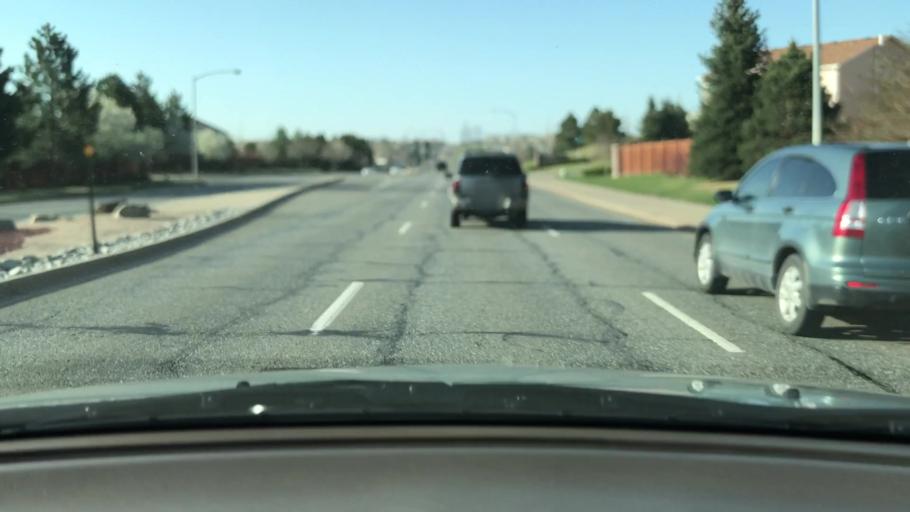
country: US
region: Colorado
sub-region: Adams County
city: Aurora
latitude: 39.6627
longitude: -104.7723
